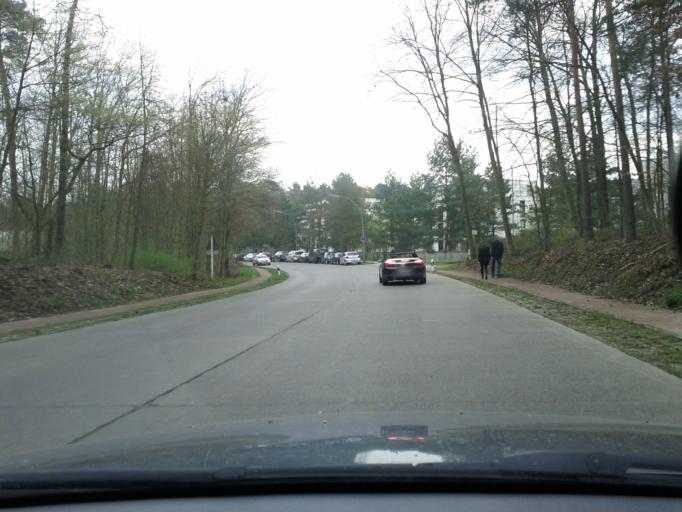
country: DE
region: Berlin
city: Dahlem
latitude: 52.4588
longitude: 13.2623
